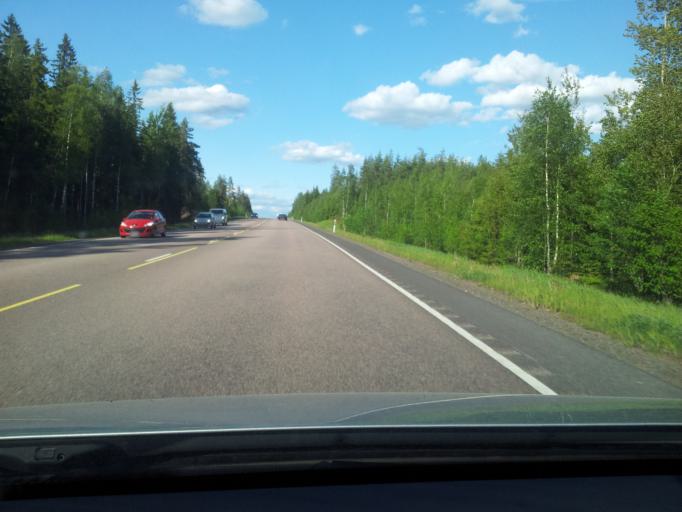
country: FI
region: Kymenlaakso
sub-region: Kouvola
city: Elimaeki
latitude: 60.7182
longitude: 26.3827
